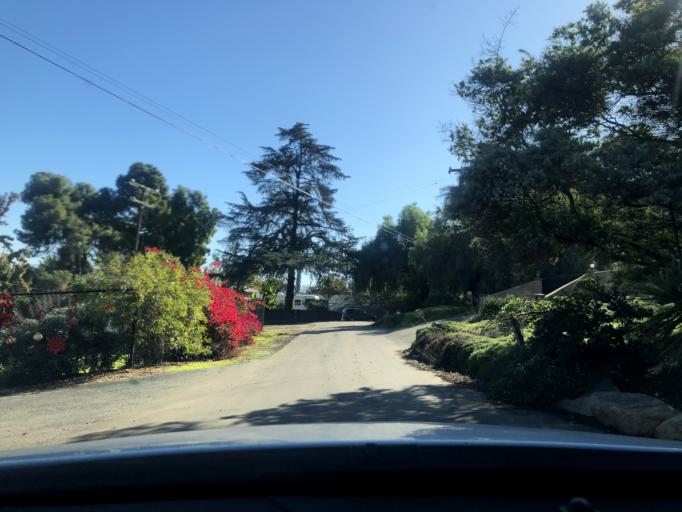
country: US
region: California
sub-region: San Diego County
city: Casa de Oro-Mount Helix
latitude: 32.7751
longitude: -116.9450
